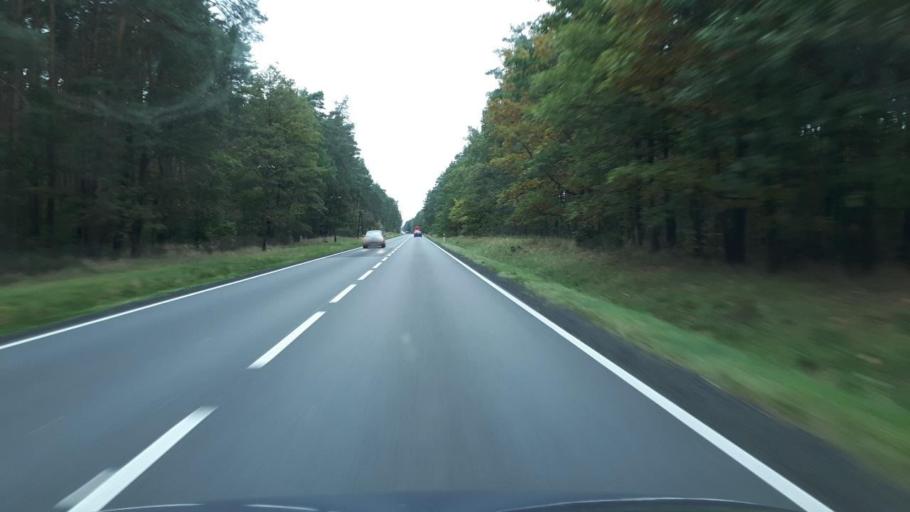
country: PL
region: Greater Poland Voivodeship
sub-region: Powiat ostrzeszowski
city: Ostrzeszow
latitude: 51.4512
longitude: 17.9074
